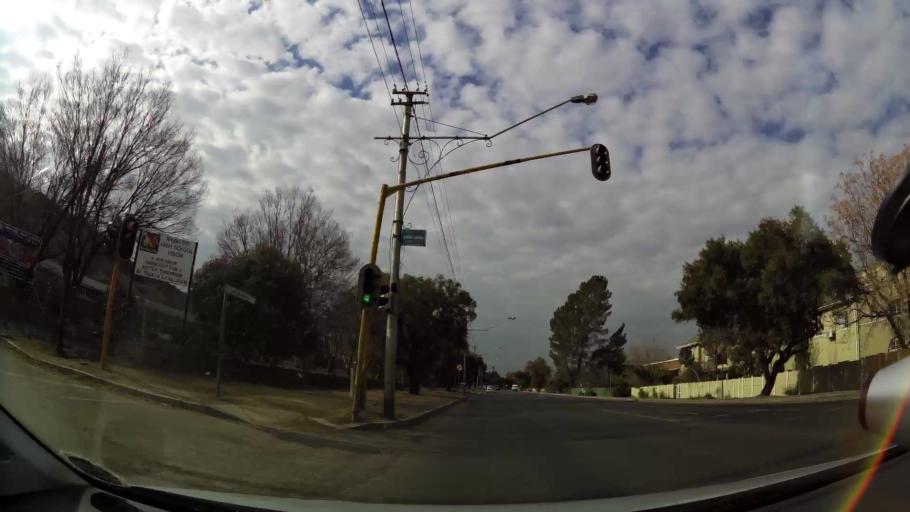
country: ZA
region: Orange Free State
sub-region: Mangaung Metropolitan Municipality
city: Bloemfontein
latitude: -29.1078
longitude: 26.2336
